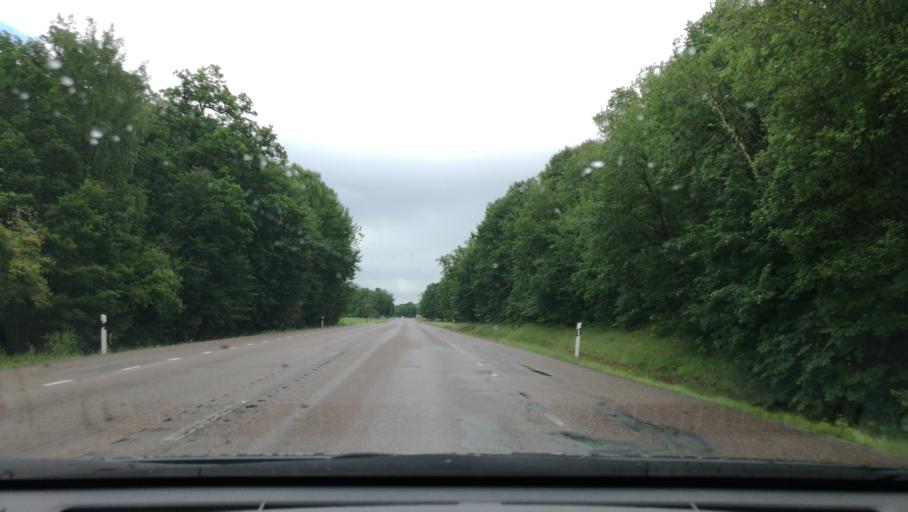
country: SE
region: Vaestmanland
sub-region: Kungsors Kommun
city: Kungsoer
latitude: 59.4375
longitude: 16.0548
